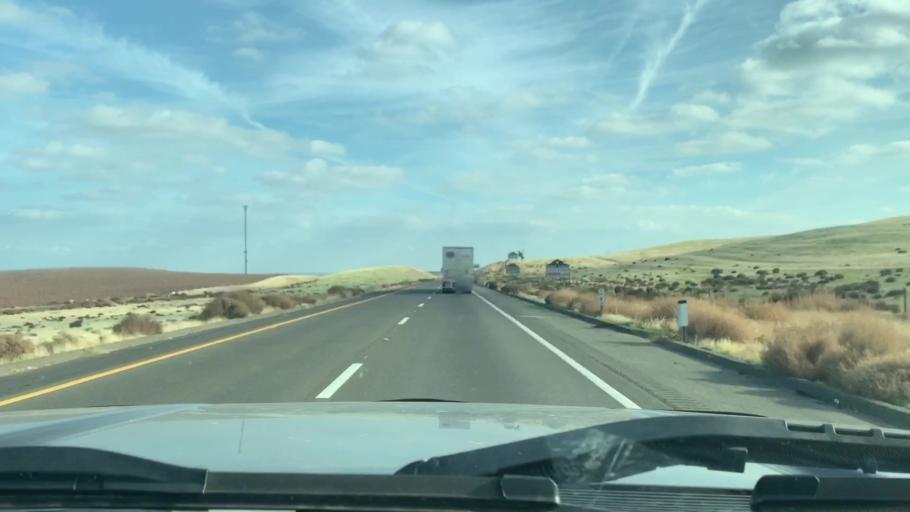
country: US
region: California
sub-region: Kings County
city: Kettleman City
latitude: 36.0171
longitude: -120.0023
